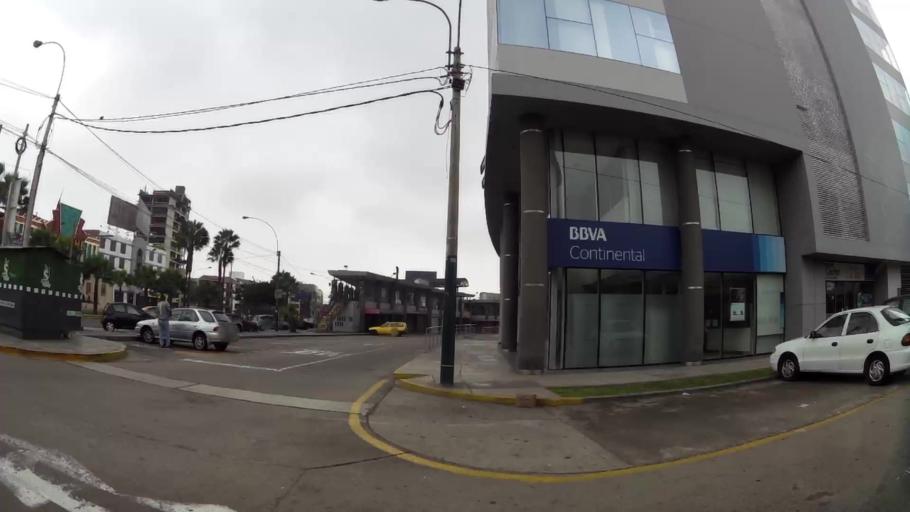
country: PE
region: Lima
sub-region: Lima
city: Surco
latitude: -12.1267
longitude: -76.9875
